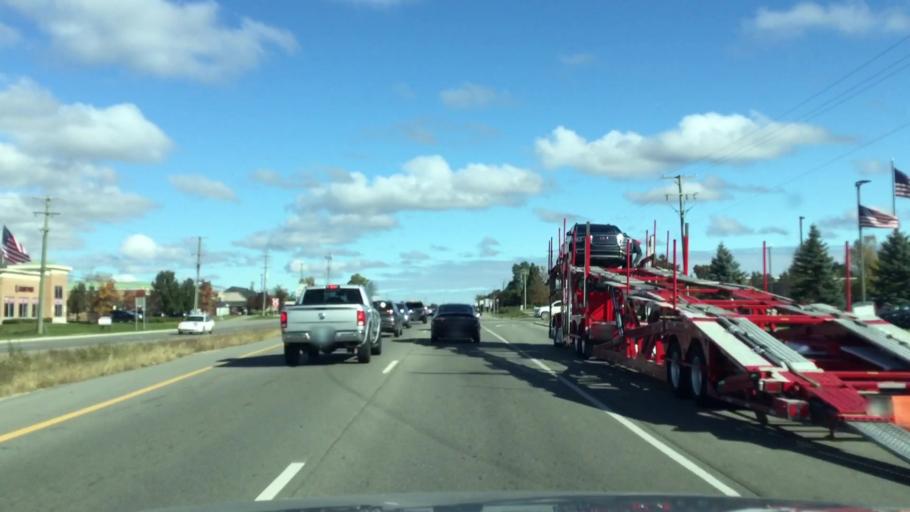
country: US
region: Michigan
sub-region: Oakland County
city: Lake Orion
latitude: 42.7597
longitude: -83.2443
